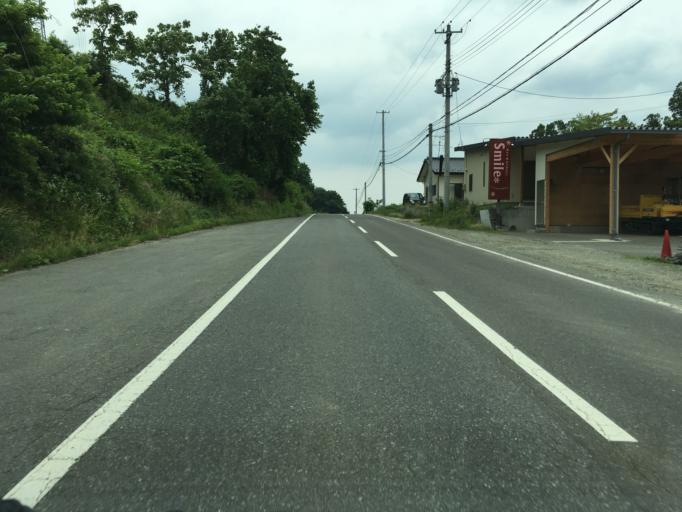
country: JP
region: Fukushima
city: Nihommatsu
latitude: 37.6240
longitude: 140.5392
